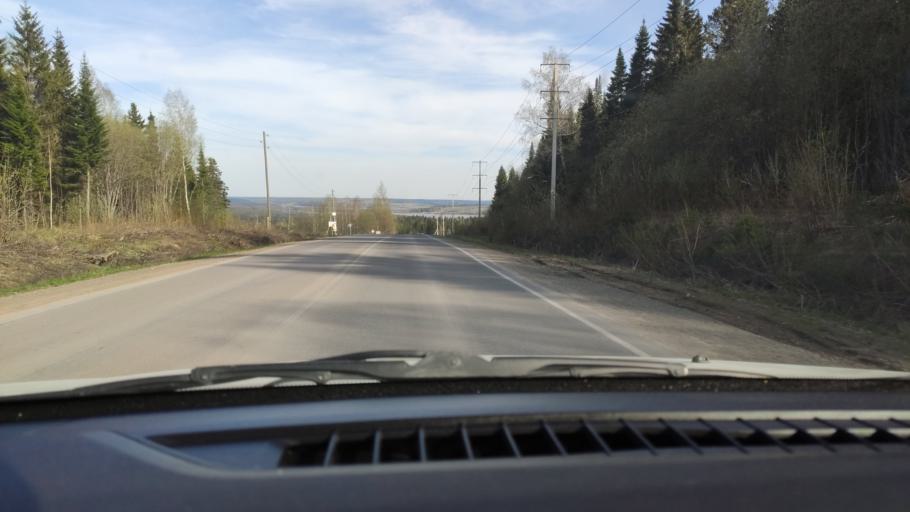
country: RU
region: Perm
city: Novyye Lyady
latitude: 57.9197
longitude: 56.6643
